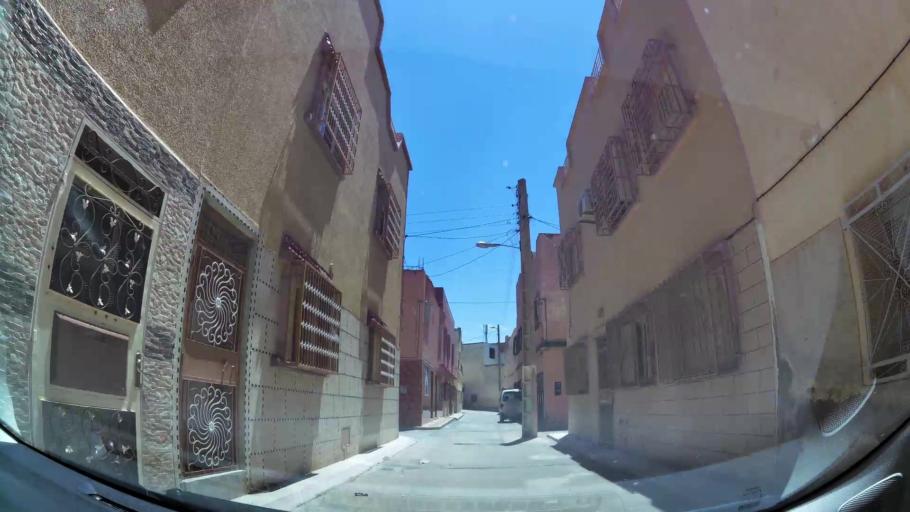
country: MA
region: Oriental
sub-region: Oujda-Angad
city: Oujda
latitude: 34.6770
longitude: -1.8794
